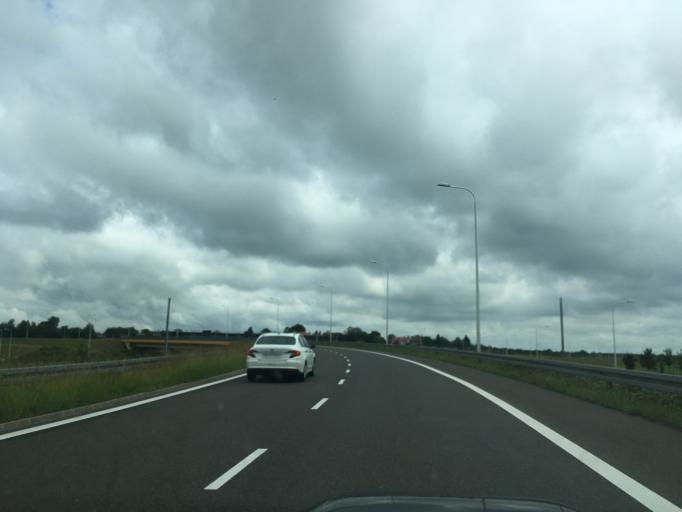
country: PL
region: Lublin Voivodeship
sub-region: Powiat lubelski
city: Jastkow
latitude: 51.2826
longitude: 22.4529
